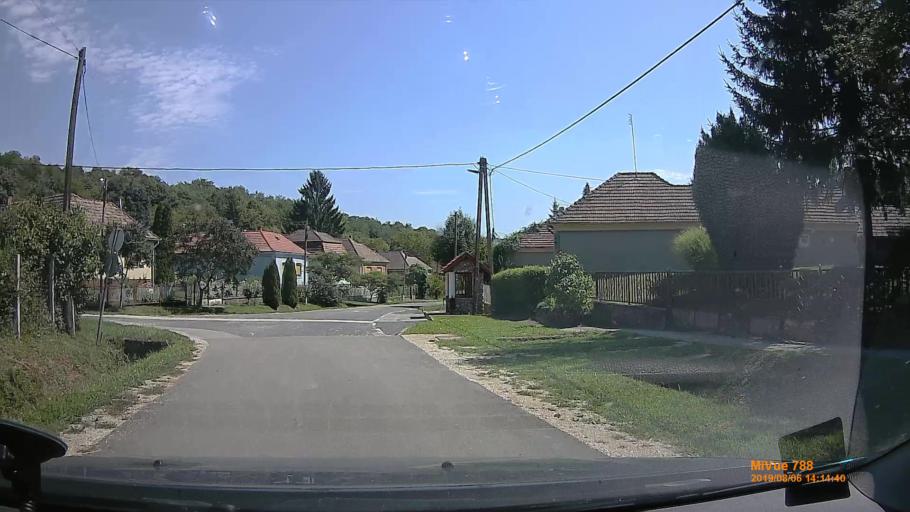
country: HU
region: Zala
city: Zalakomar
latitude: 46.5630
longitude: 17.0770
